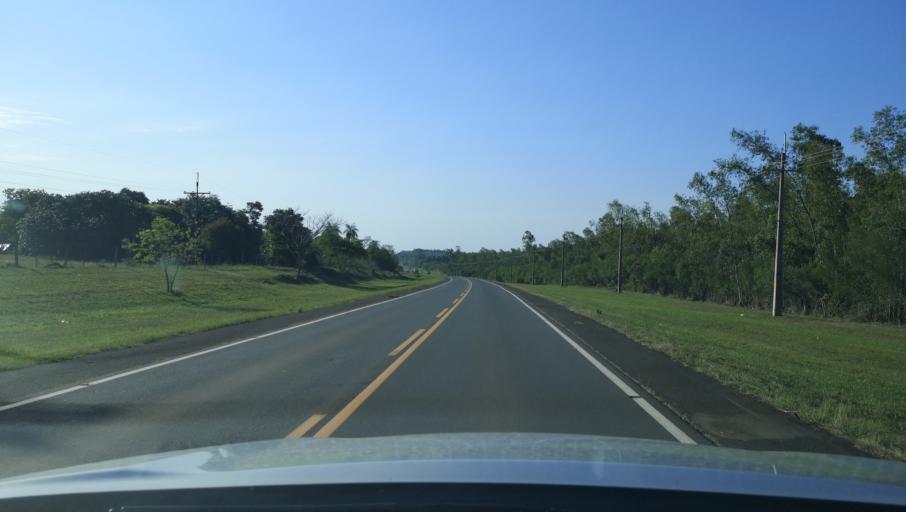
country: PY
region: Misiones
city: Santa Maria
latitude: -26.7597
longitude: -57.0343
